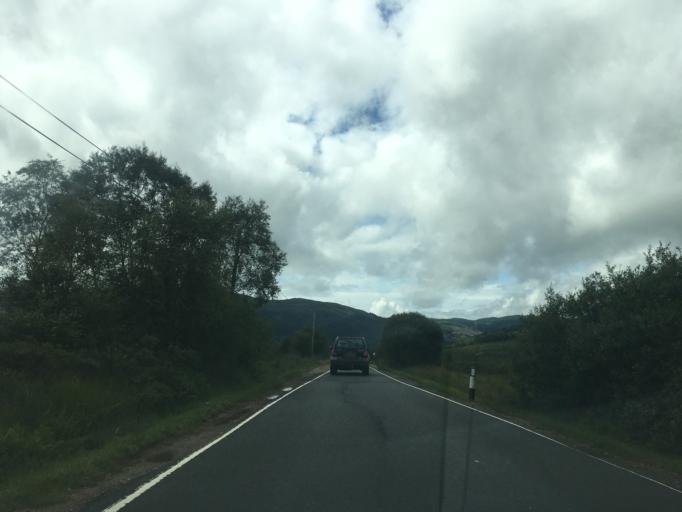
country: GB
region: Scotland
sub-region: Argyll and Bute
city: Port Bannatyne
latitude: 55.9880
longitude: -5.1586
